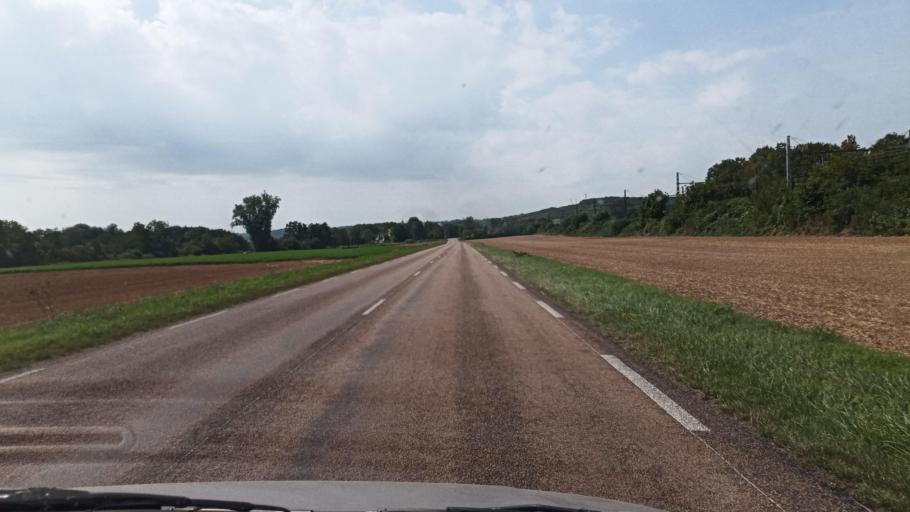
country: FR
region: Bourgogne
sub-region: Departement de l'Yonne
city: Veron
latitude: 48.1189
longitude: 3.2735
